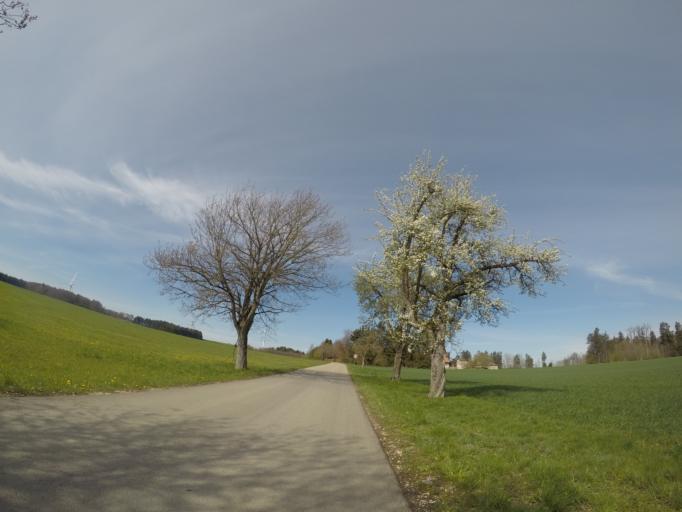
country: DE
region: Baden-Wuerttemberg
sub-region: Regierungsbezirk Stuttgart
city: Hohenstadt
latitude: 48.5402
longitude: 9.6413
